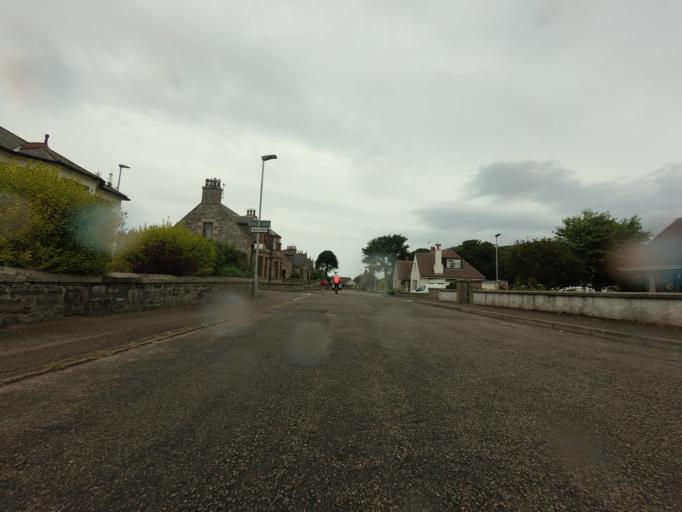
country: GB
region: Scotland
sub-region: Moray
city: Cullen
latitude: 57.6879
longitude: -2.8185
